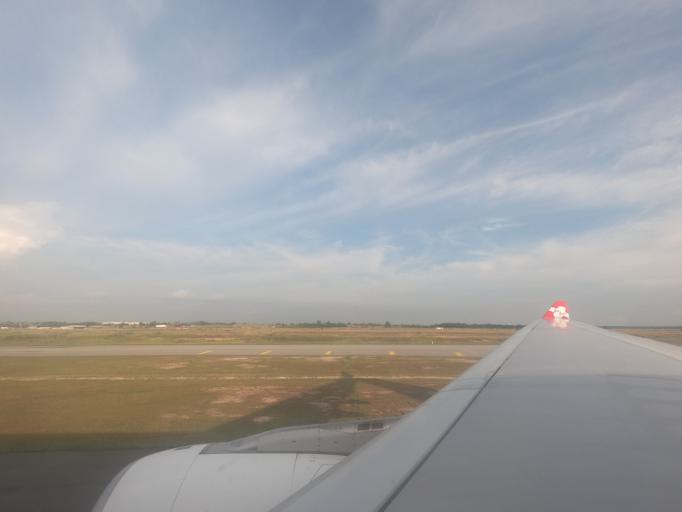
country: MY
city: Sungai Pelek New Village
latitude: 2.7375
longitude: 101.6890
